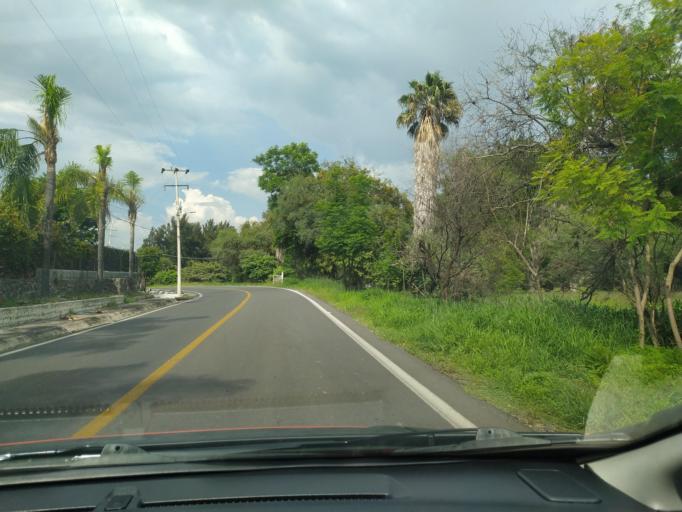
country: MX
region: Jalisco
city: Villa Corona
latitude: 20.4101
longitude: -103.6801
